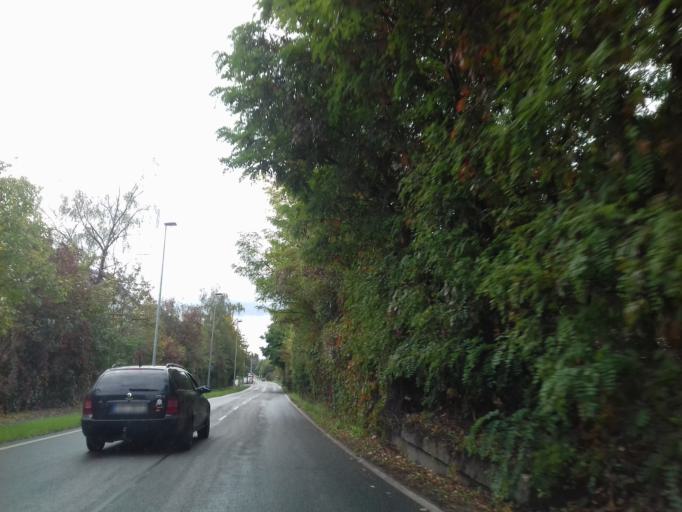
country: CZ
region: Praha
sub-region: Praha 12
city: Modrany
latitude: 49.9917
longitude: 14.3720
